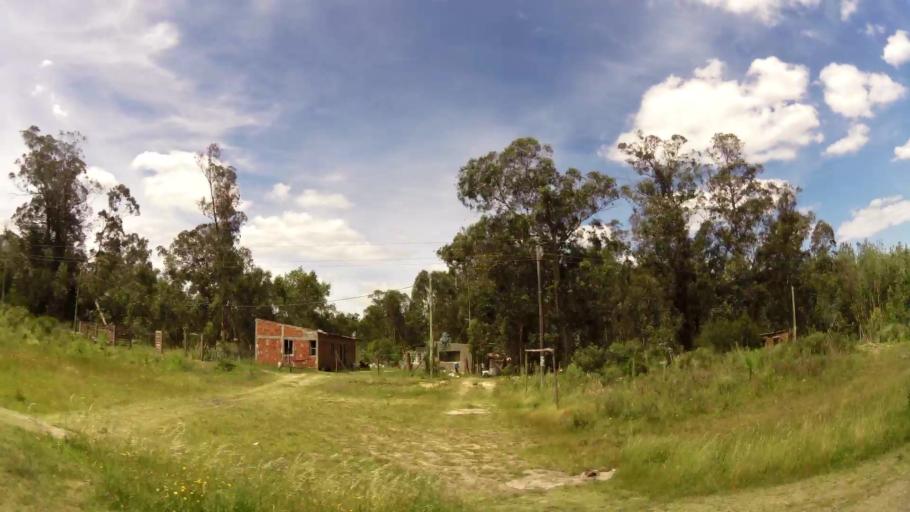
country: UY
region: Canelones
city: Empalme Olmos
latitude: -34.7803
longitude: -55.8870
